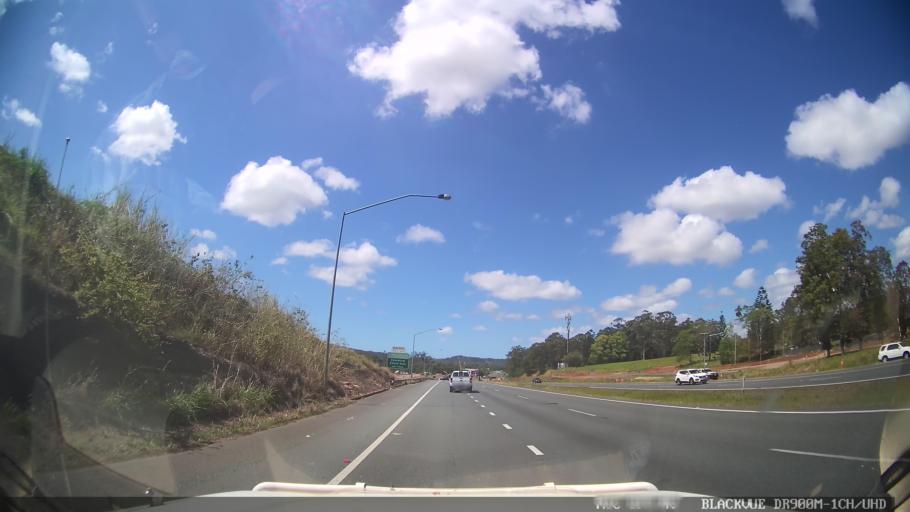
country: AU
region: Queensland
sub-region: Sunshine Coast
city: Woombye
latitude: -26.6759
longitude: 153.0004
